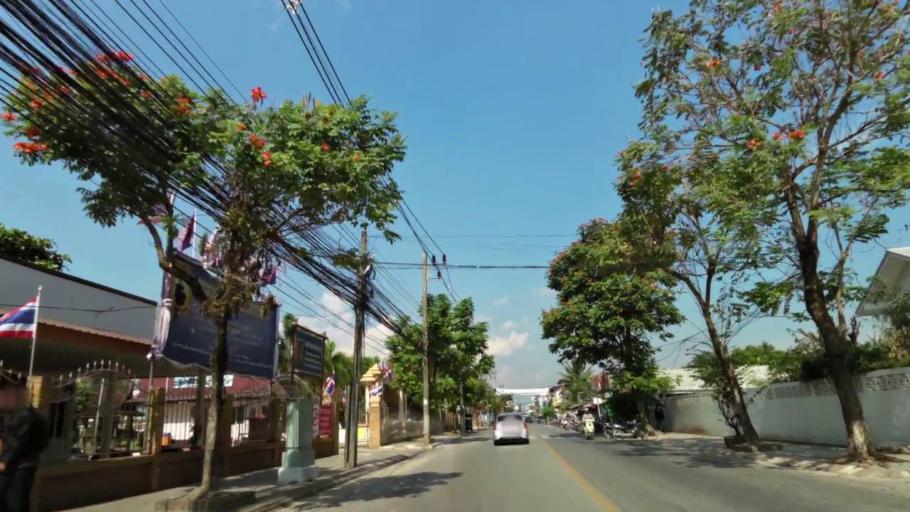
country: TH
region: Chiang Rai
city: Chiang Rai
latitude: 19.9028
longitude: 99.8283
